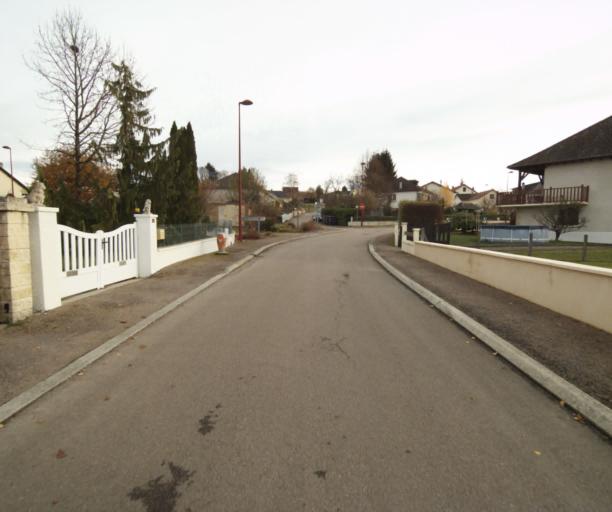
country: FR
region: Limousin
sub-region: Departement de la Correze
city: Sainte-Fortunade
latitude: 45.2145
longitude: 1.7683
